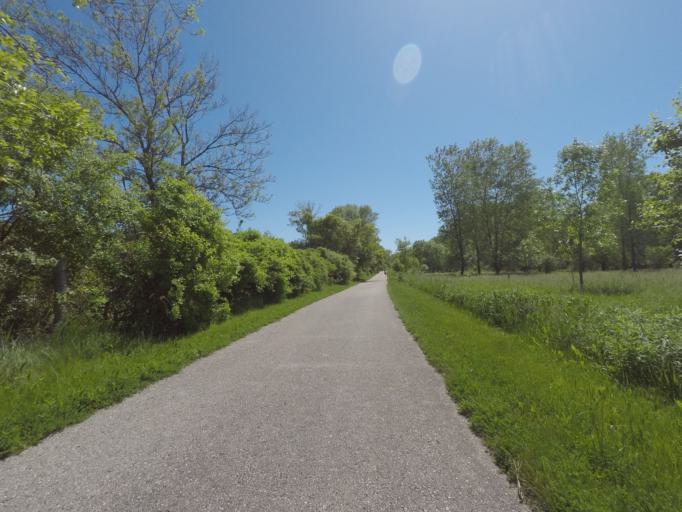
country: US
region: Wisconsin
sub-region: Sheboygan County
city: Kohler
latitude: 43.7530
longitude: -87.7754
